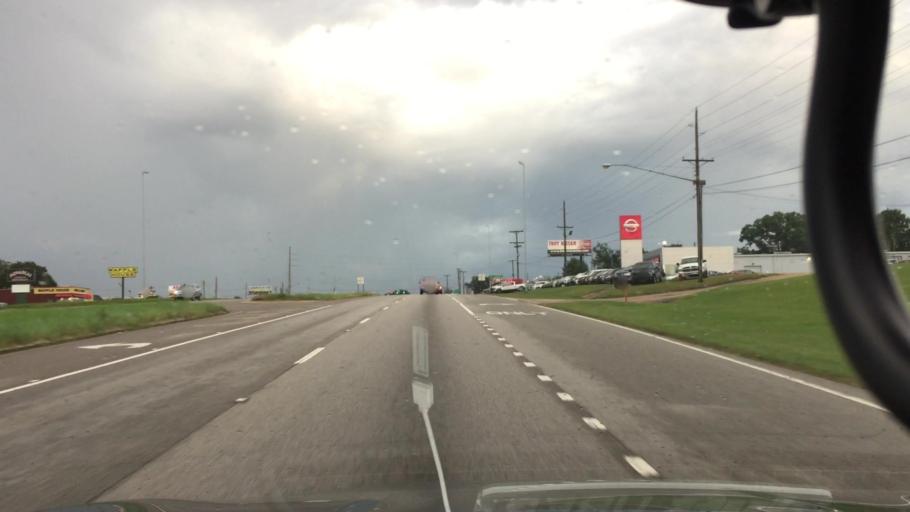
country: US
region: Alabama
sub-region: Pike County
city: Troy
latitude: 31.7952
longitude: -85.9804
